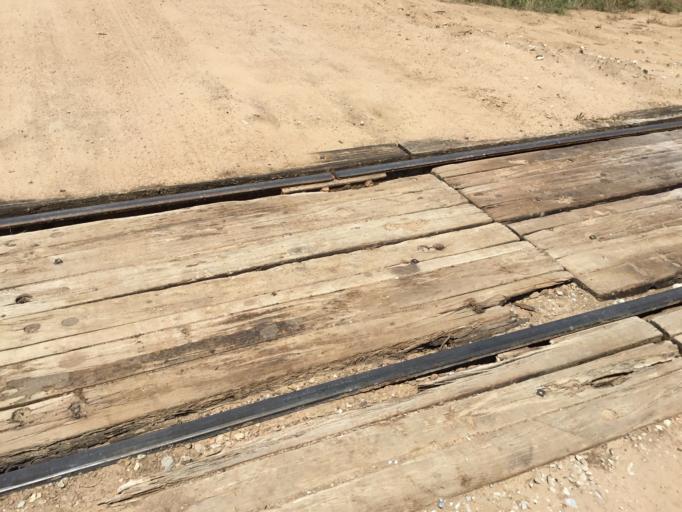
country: US
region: Kansas
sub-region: Kingman County
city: Kingman
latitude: 37.5749
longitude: -98.1330
